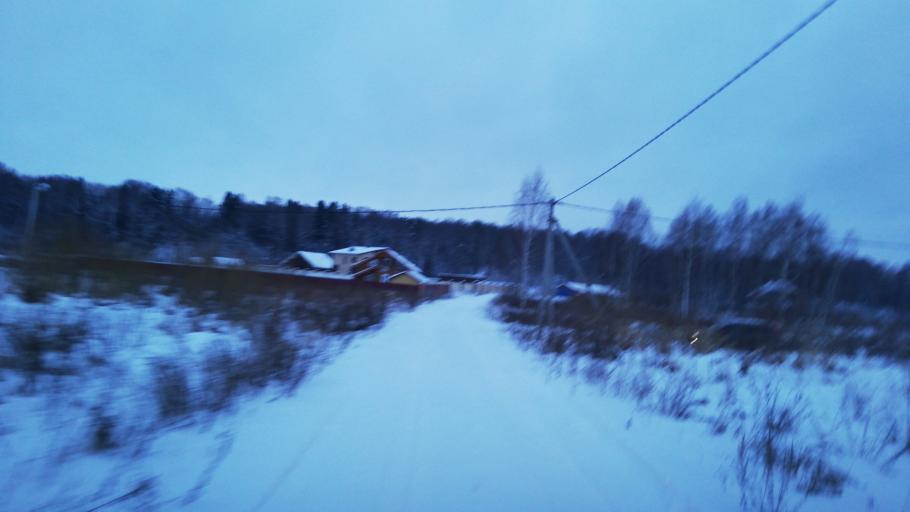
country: RU
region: Jaroslavl
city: Krasnyye Tkachi
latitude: 57.4428
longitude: 39.7966
